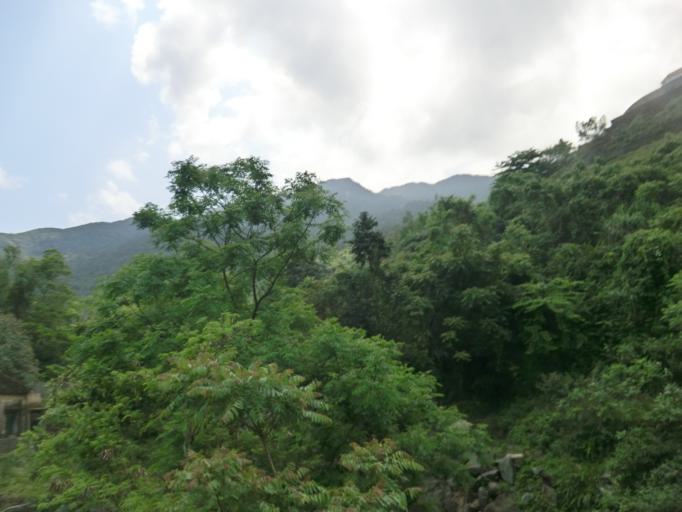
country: VN
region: Da Nang
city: Lien Chieu
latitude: 16.2042
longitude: 108.1112
